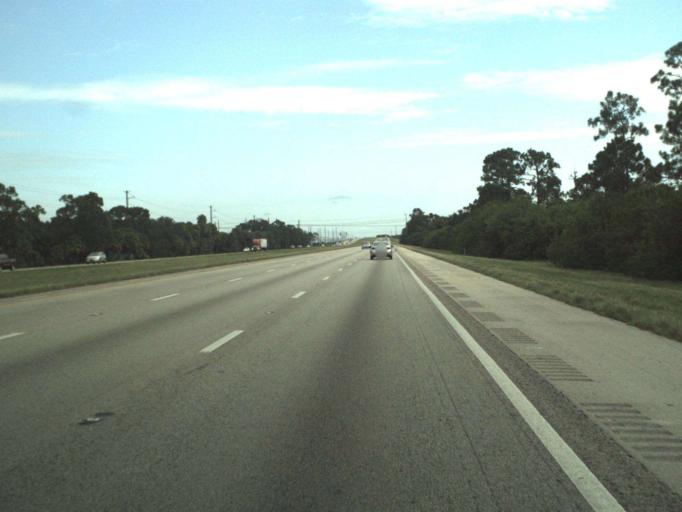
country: US
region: Florida
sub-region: Saint Lucie County
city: River Park
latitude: 27.3412
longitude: -80.4139
